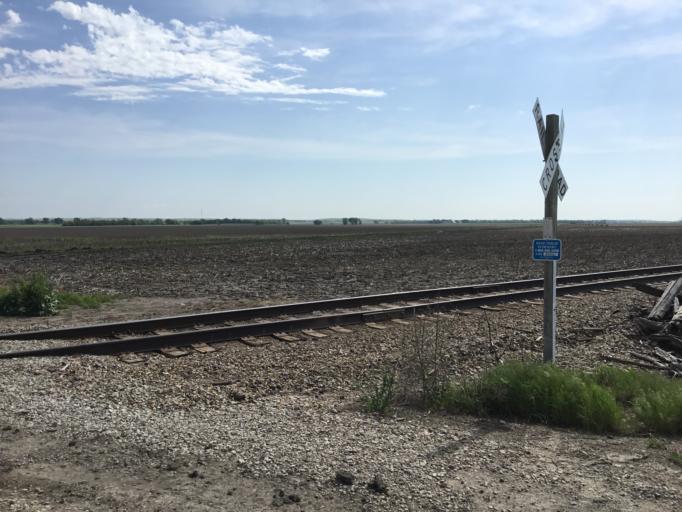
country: US
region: Kansas
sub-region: Mitchell County
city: Beloit
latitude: 39.3930
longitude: -97.9483
